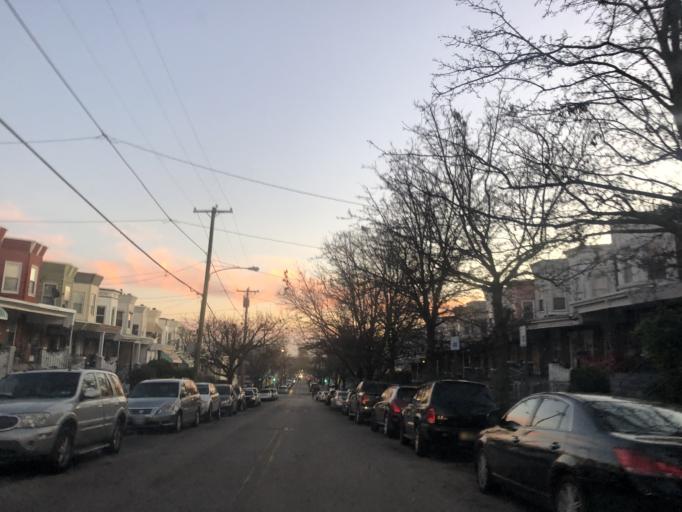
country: US
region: Pennsylvania
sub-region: Delaware County
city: Millbourne
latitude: 39.9771
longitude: -75.2405
